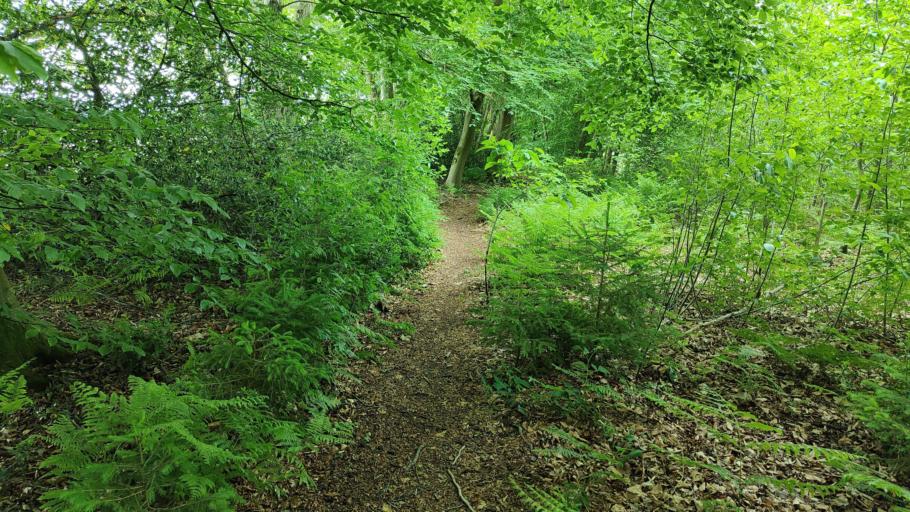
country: BE
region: Wallonia
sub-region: Province de Liege
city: La Calamine
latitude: 50.7188
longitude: 6.0645
